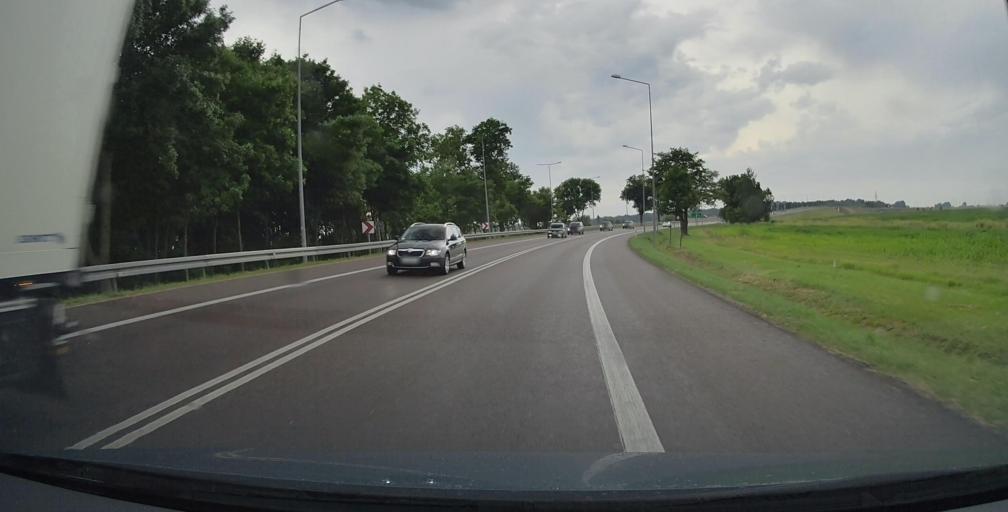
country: PL
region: Lublin Voivodeship
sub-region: Powiat bialski
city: Miedzyrzec Podlaski
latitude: 52.0005
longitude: 22.7599
